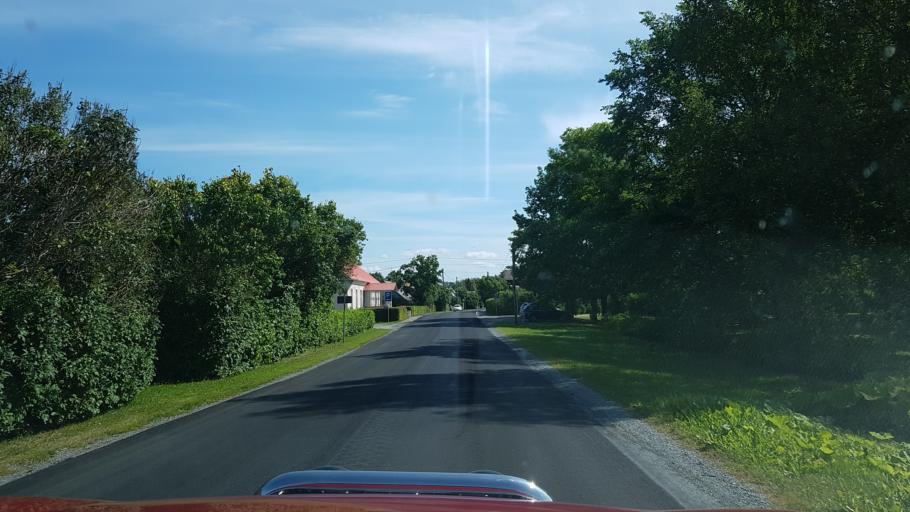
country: EE
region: Laeaene-Virumaa
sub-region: Tapa vald
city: Tapa
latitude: 59.1937
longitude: 25.8261
